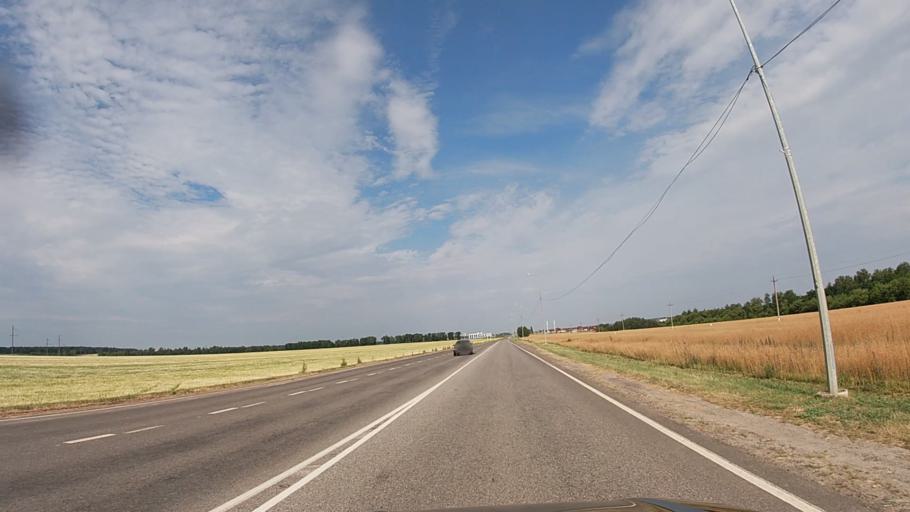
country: RU
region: Belgorod
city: Krasnaya Yaruga
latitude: 50.7962
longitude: 35.7087
